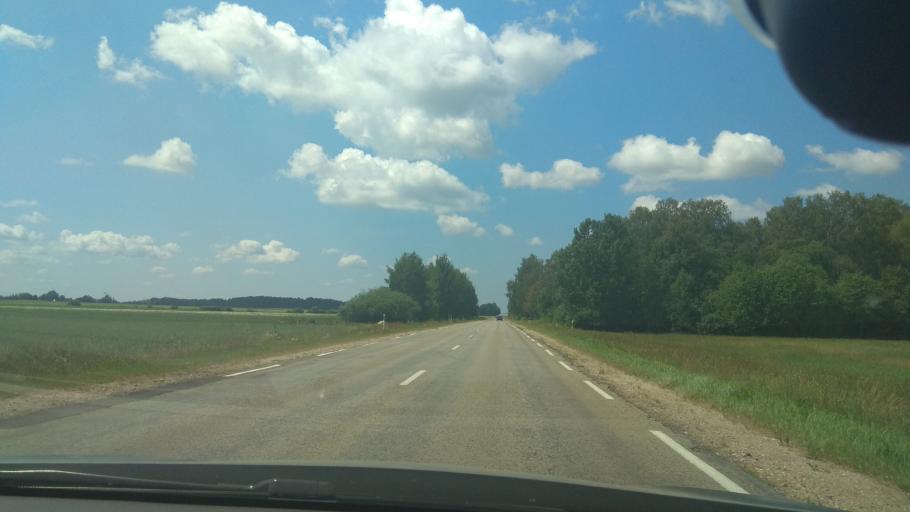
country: LT
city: Naujoji Akmene
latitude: 56.2887
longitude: 22.9589
